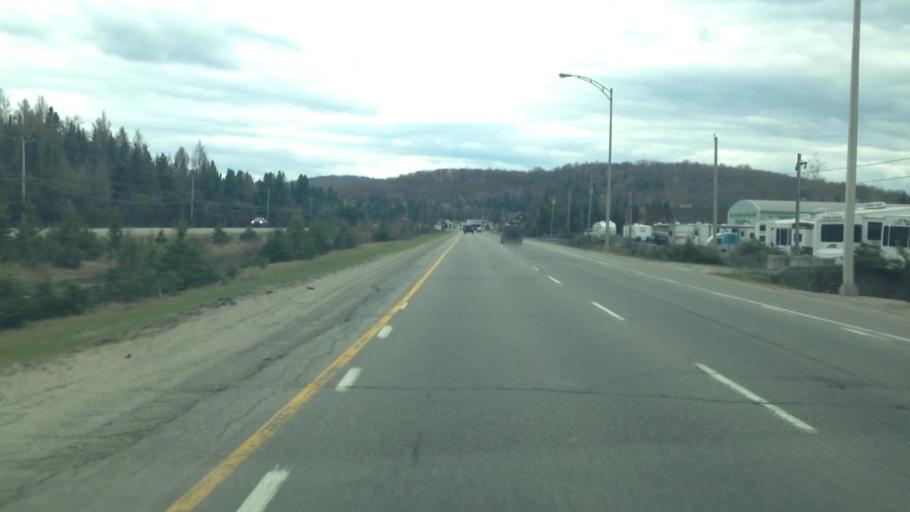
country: CA
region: Quebec
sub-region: Laurentides
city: Sainte-Agathe-des-Monts
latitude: 46.0718
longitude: -74.3142
